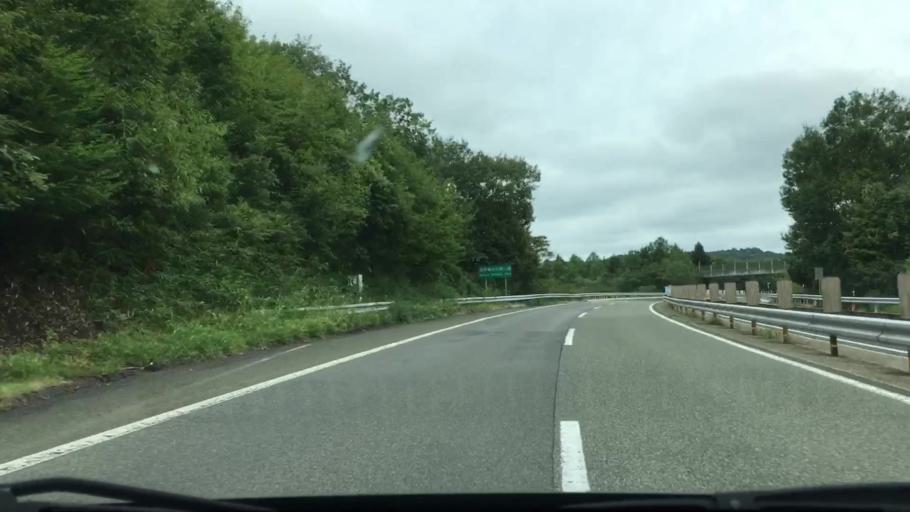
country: JP
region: Hiroshima
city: Shobara
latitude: 34.8420
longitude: 133.0045
